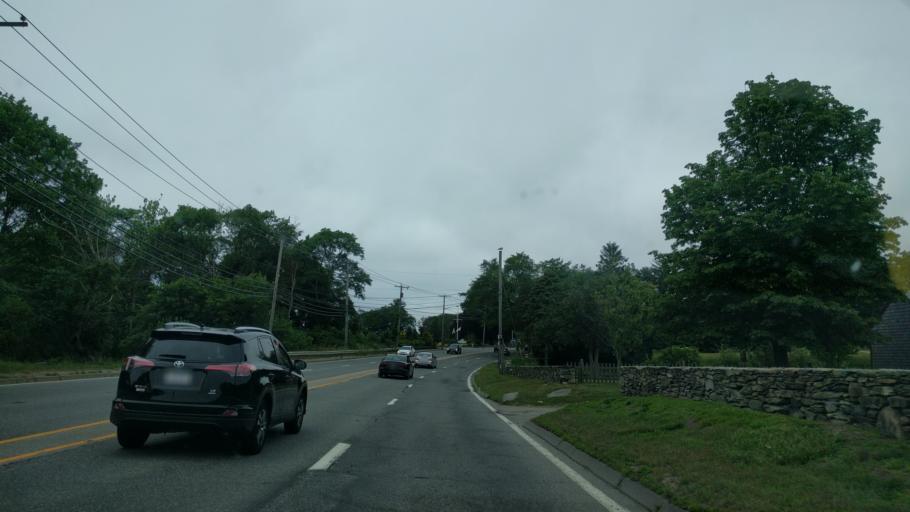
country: US
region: Rhode Island
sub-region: Newport County
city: Middletown
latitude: 41.5532
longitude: -71.2911
